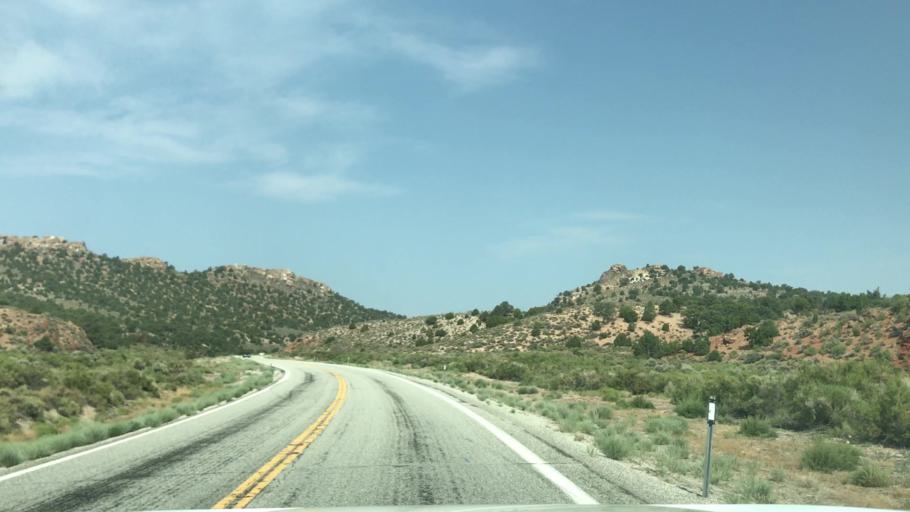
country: US
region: Nevada
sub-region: White Pine County
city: McGill
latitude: 39.1159
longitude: -114.2773
